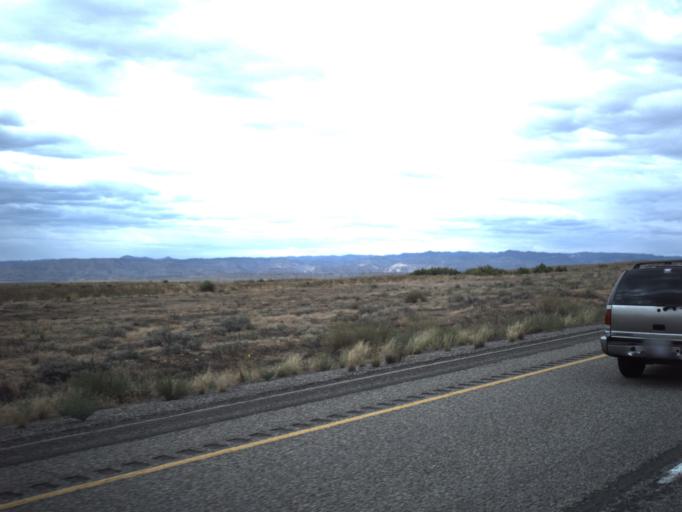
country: US
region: Colorado
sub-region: Mesa County
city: Loma
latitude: 39.1404
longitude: -109.1547
